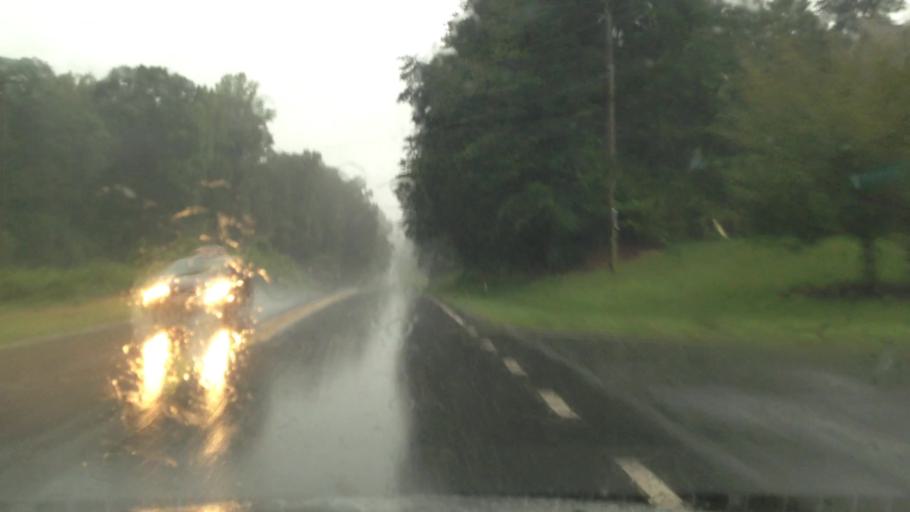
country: US
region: North Carolina
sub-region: Guilford County
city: Summerfield
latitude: 36.2664
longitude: -79.8517
